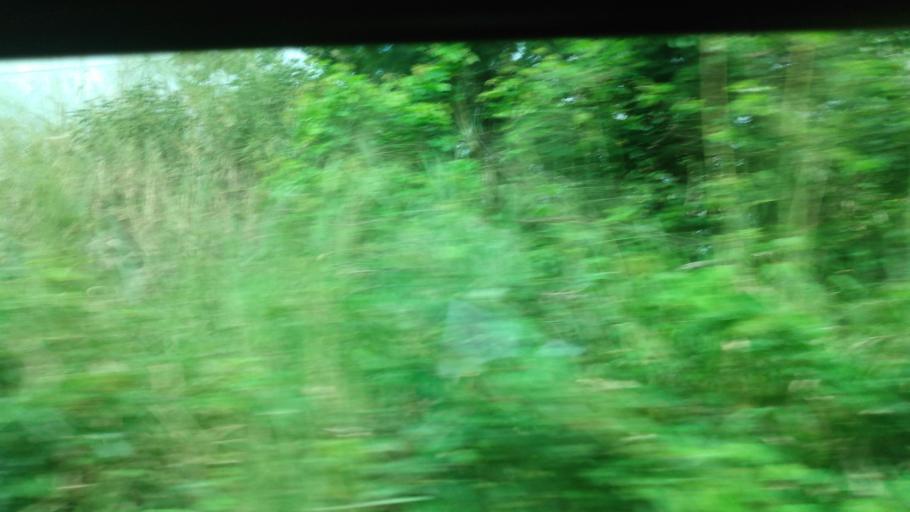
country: BR
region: Pernambuco
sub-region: Maraial
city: Maraial
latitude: -8.7849
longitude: -35.8773
